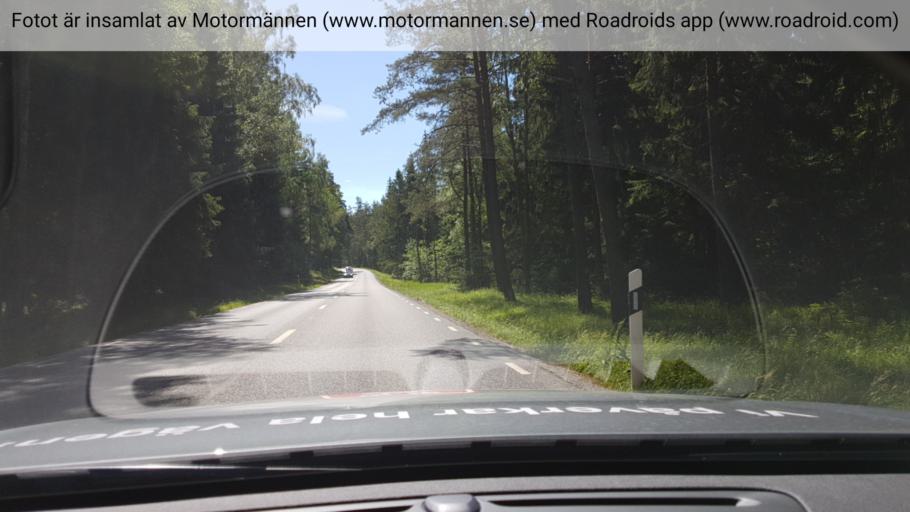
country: SE
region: Stockholm
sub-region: Haninge Kommun
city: Haninge
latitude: 59.1491
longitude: 18.1797
